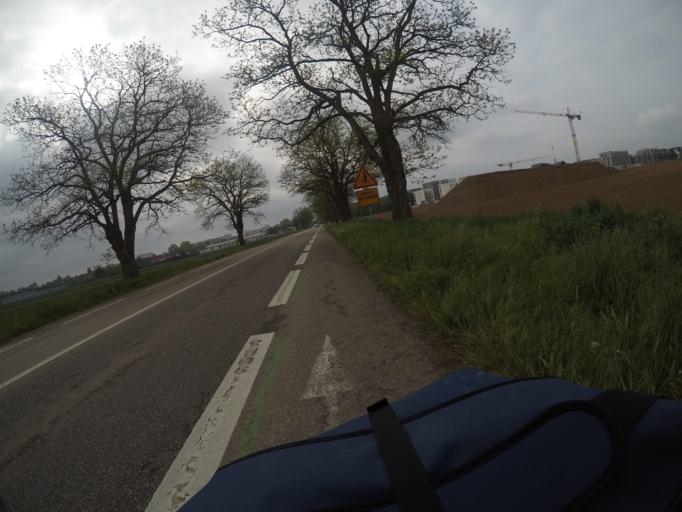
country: FR
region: Alsace
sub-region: Departement du Bas-Rhin
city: Oberhausbergen
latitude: 48.6076
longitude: 7.7017
